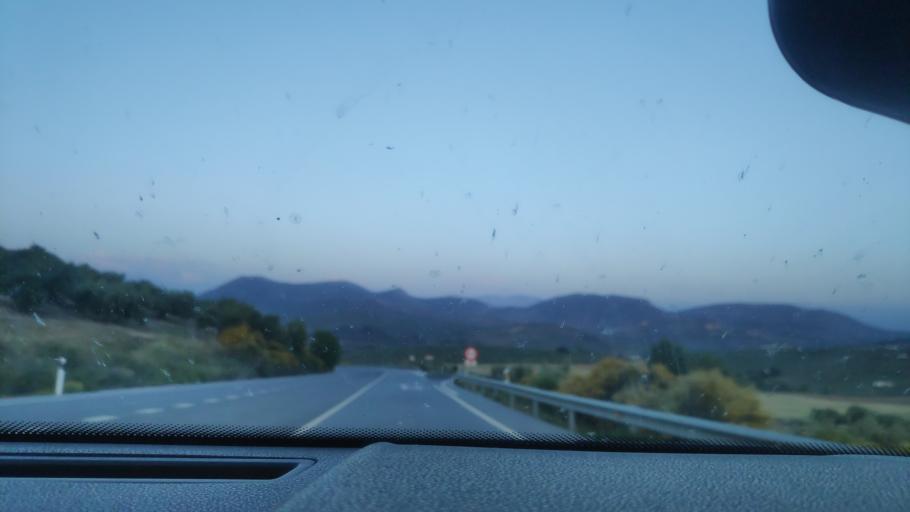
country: ES
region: Andalusia
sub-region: Provincia de Granada
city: Benalua de las Villas
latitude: 37.4283
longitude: -3.7501
